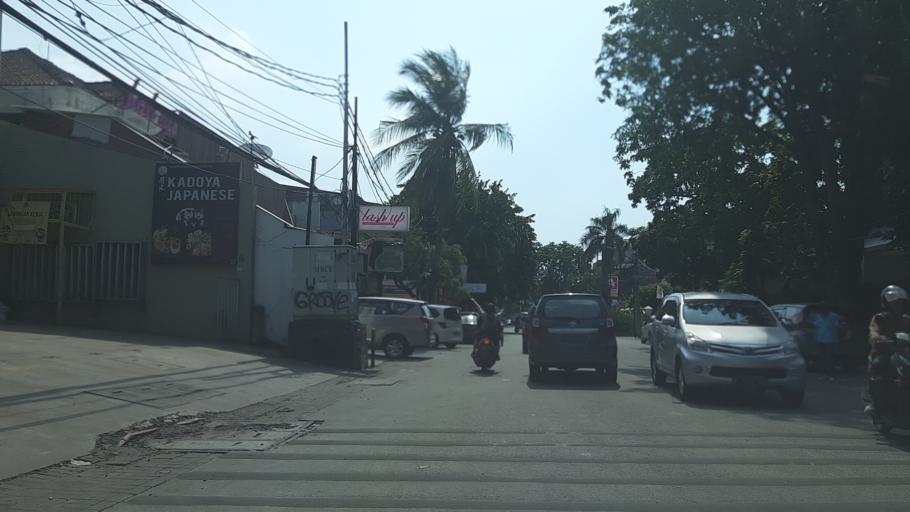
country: ID
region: Jakarta Raya
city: Jakarta
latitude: -6.1695
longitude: 106.7727
